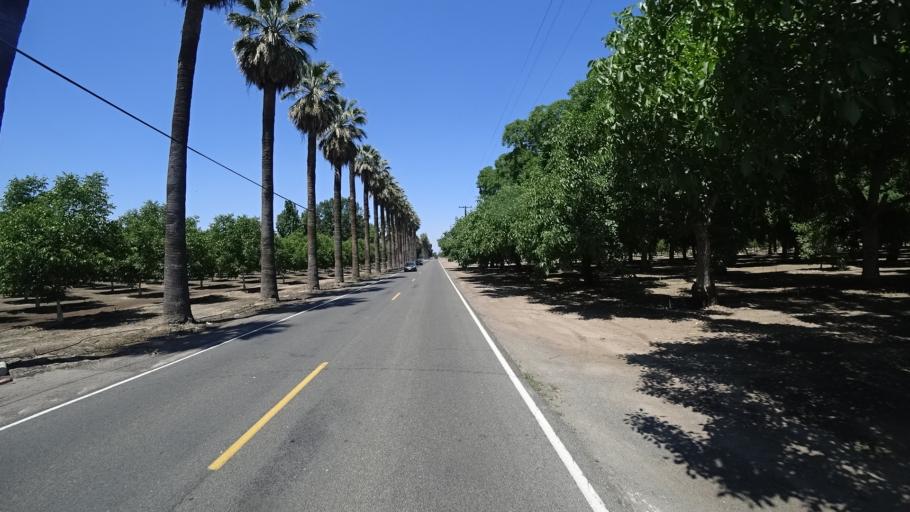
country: US
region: California
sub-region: Kings County
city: Lucerne
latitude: 36.3936
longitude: -119.6550
